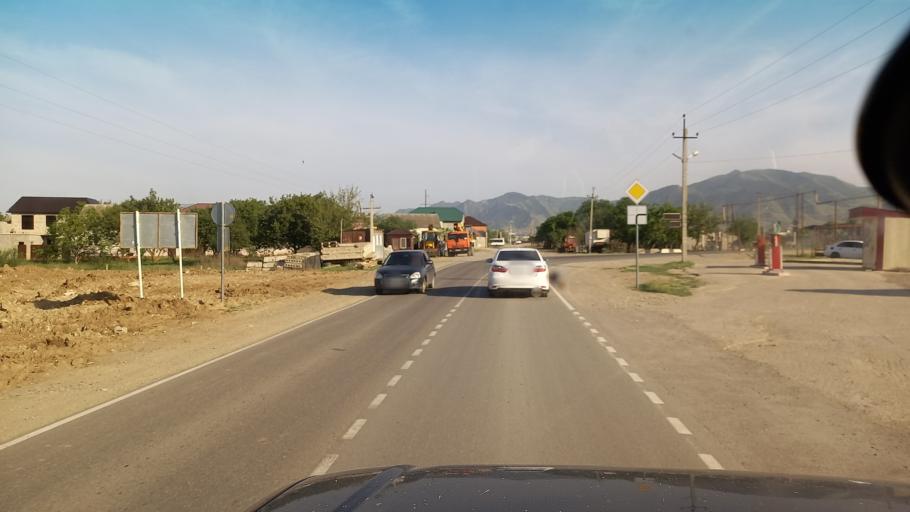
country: RU
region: Dagestan
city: Shamkhal-Termen
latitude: 43.0060
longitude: 47.3338
